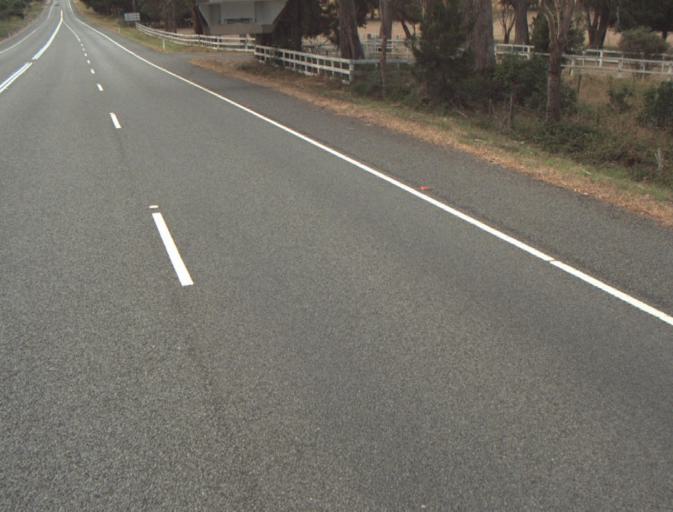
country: AU
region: Tasmania
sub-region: Launceston
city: Mayfield
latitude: -41.2763
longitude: 147.0370
